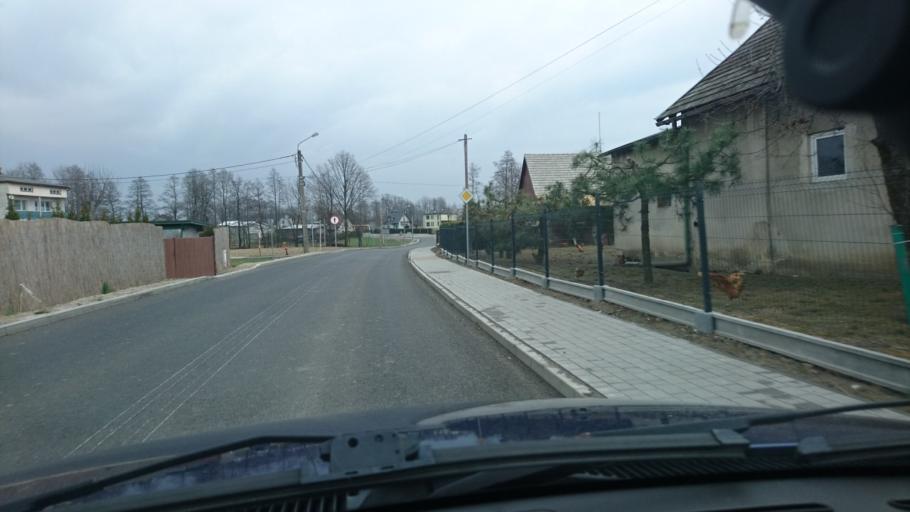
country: PL
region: Silesian Voivodeship
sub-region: Powiat bielski
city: Bronow
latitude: 49.8781
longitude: 18.9231
